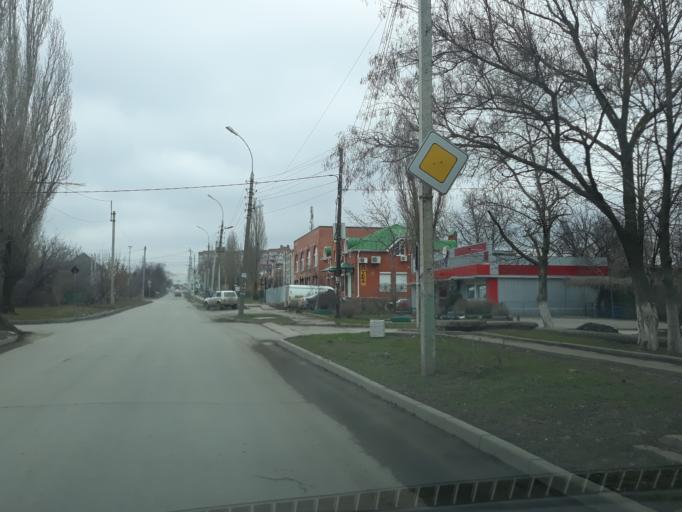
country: RU
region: Rostov
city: Taganrog
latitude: 47.2711
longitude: 38.9307
